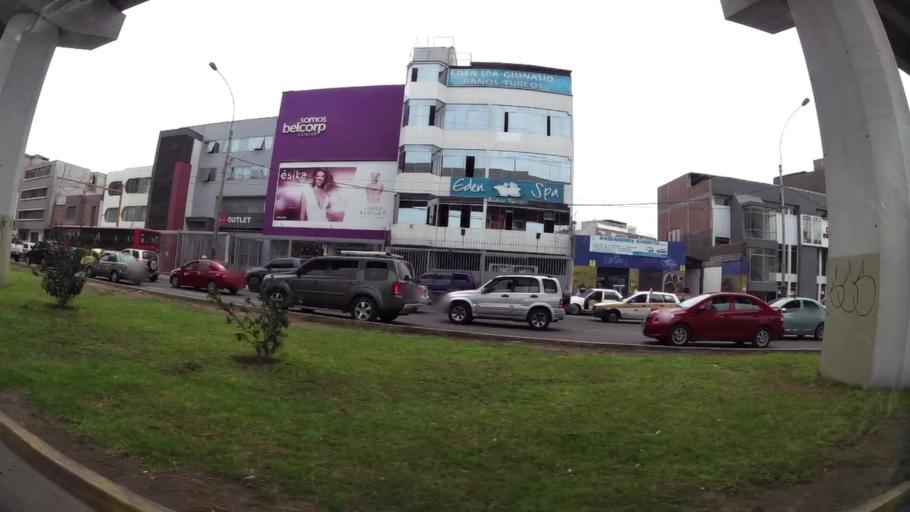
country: PE
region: Lima
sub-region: Lima
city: Surco
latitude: -12.1357
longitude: -76.9964
